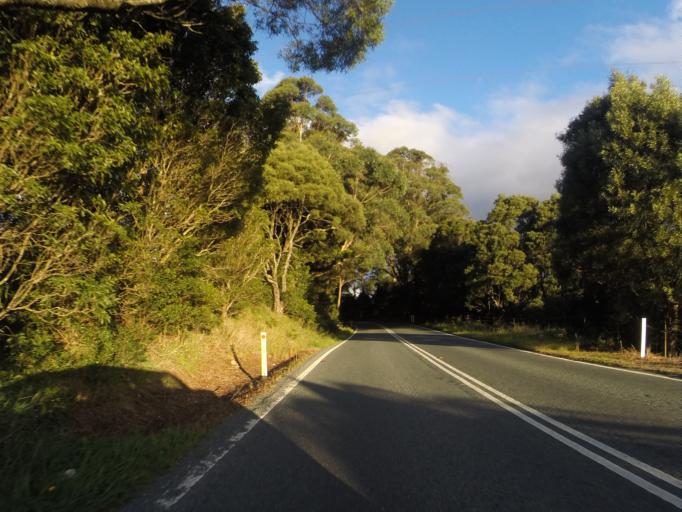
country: AU
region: New South Wales
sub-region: Shellharbour
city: Calderwood
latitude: -34.5617
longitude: 150.6256
